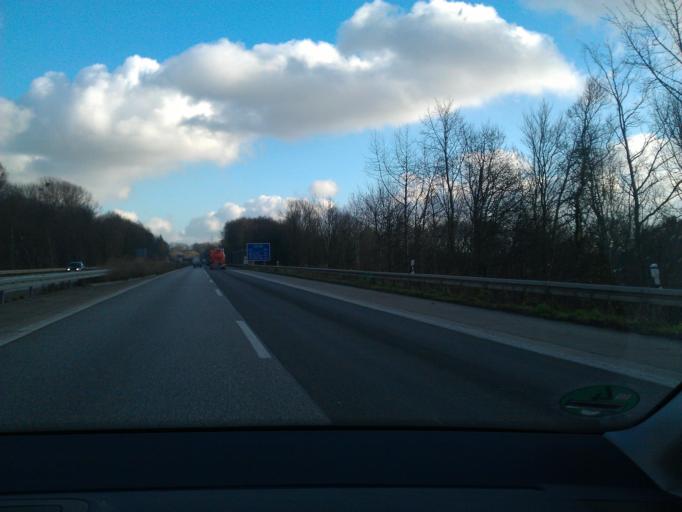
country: DE
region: North Rhine-Westphalia
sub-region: Regierungsbezirk Koln
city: Wurselen
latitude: 50.8040
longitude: 6.1159
